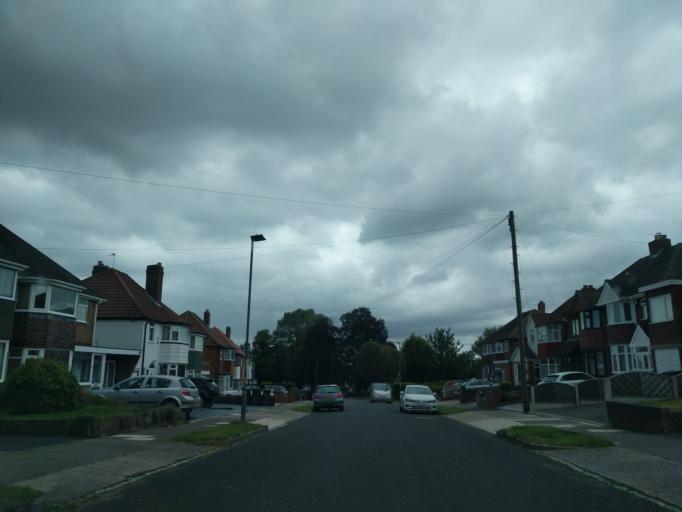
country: GB
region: England
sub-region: City and Borough of Birmingham
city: Acocks Green
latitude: 52.4630
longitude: -1.7956
